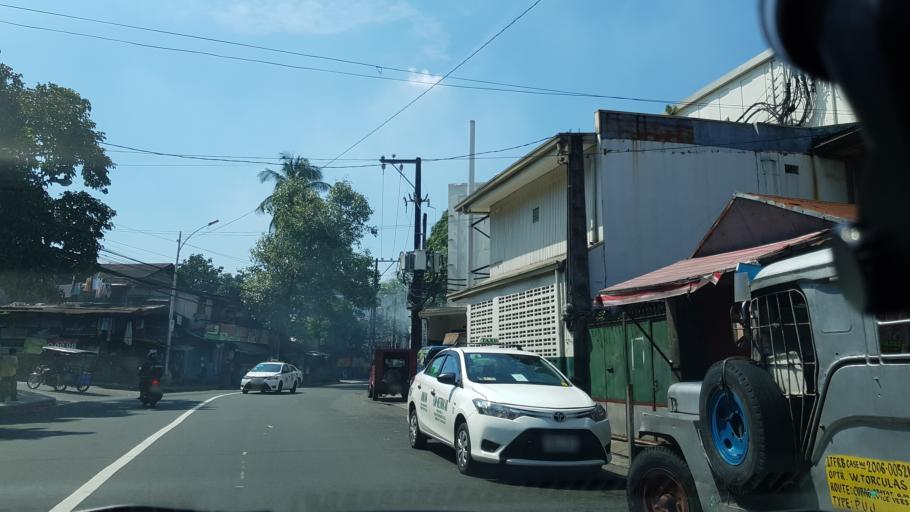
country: PH
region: Metro Manila
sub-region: San Juan
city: San Juan
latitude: 14.6196
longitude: 121.0479
